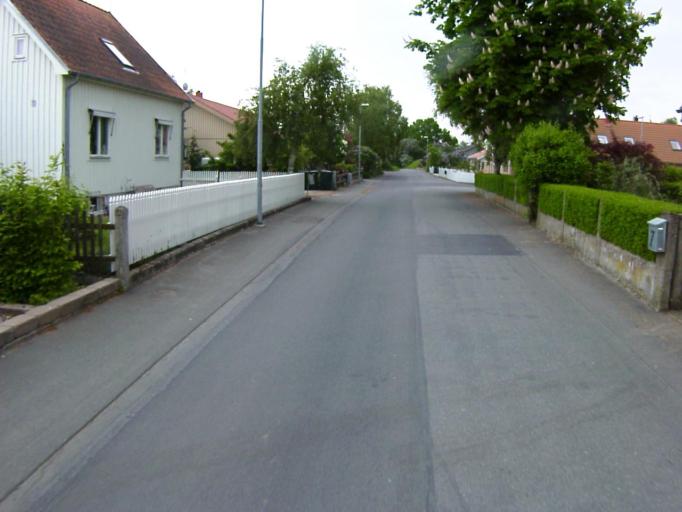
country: SE
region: Skane
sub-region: Kristianstads Kommun
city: Ahus
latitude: 55.9192
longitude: 14.2826
